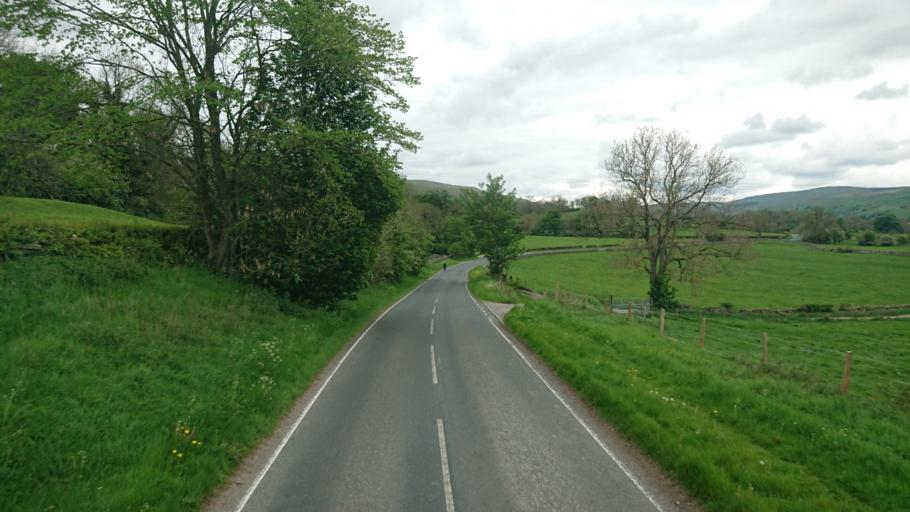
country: GB
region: England
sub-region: North Yorkshire
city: Leyburn
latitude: 54.2775
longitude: -1.9771
